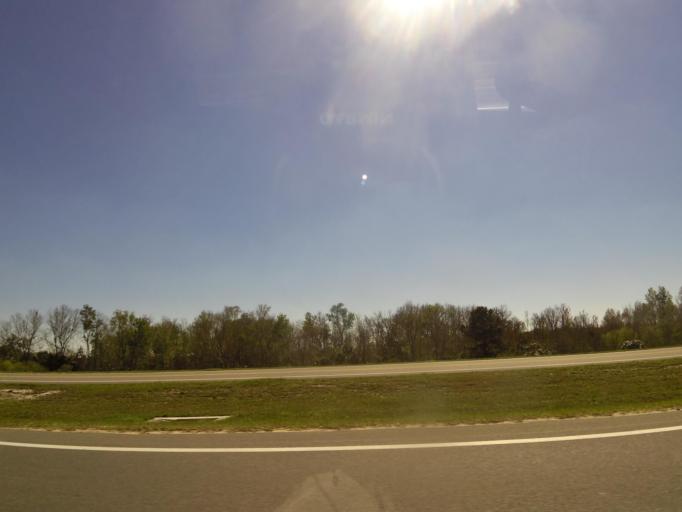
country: US
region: Florida
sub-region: Seminole County
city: Heathrow
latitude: 28.8118
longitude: -81.4398
